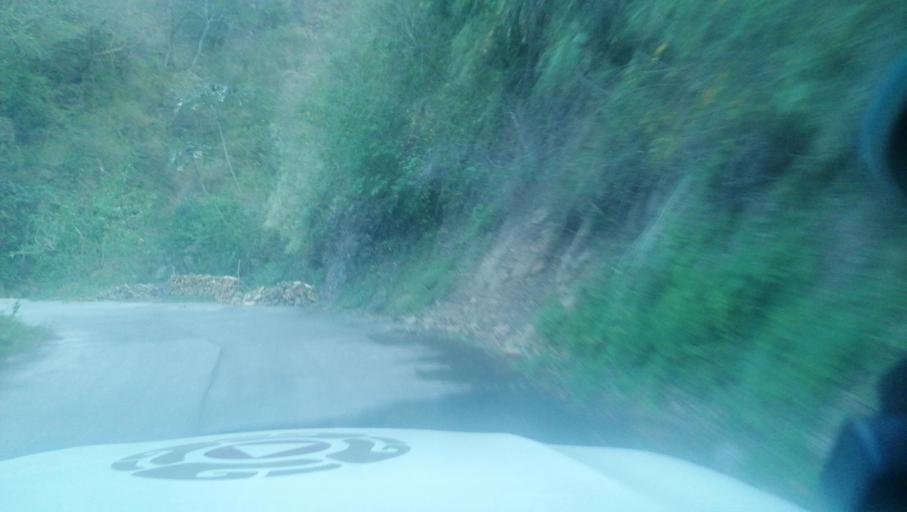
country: MX
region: Chiapas
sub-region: Cacahoatan
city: Benito Juarez
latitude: 15.1412
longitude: -92.1966
